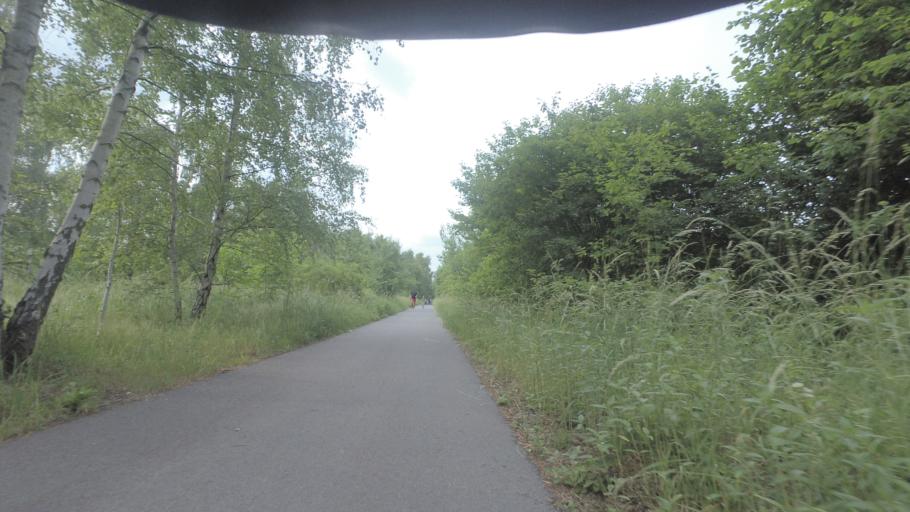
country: DE
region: Berlin
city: Gropiusstadt
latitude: 52.4175
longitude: 13.4684
